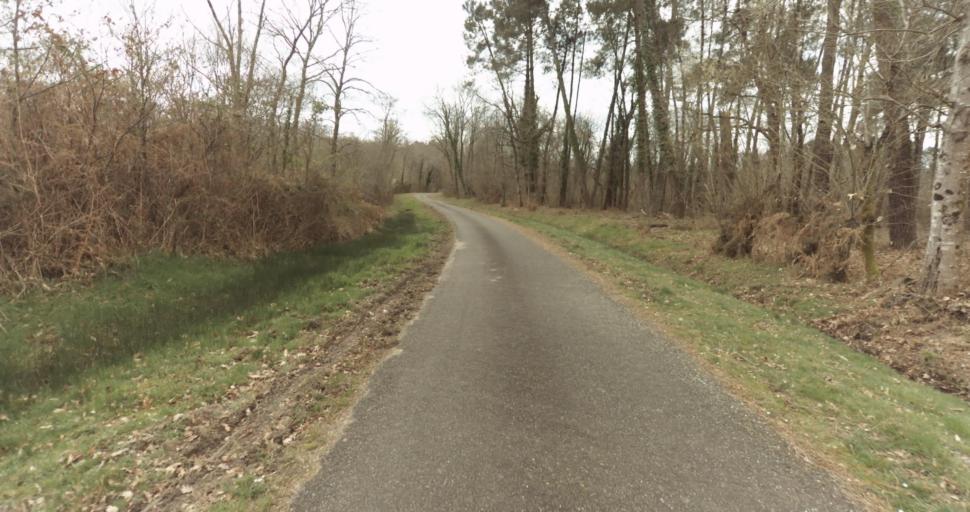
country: FR
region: Aquitaine
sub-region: Departement des Landes
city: Roquefort
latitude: 44.0781
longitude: -0.3901
